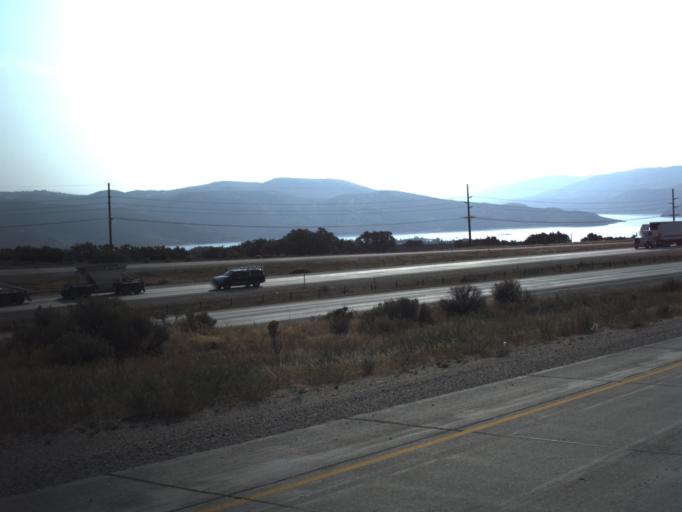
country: US
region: Utah
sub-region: Summit County
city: Park City
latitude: 40.6235
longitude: -111.4404
